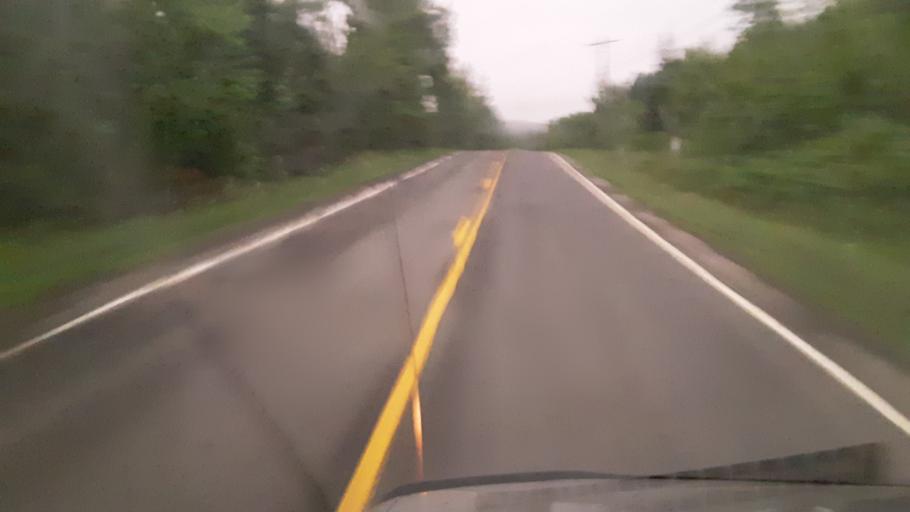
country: US
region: Maine
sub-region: Penobscot County
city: Patten
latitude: 46.1084
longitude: -68.4140
